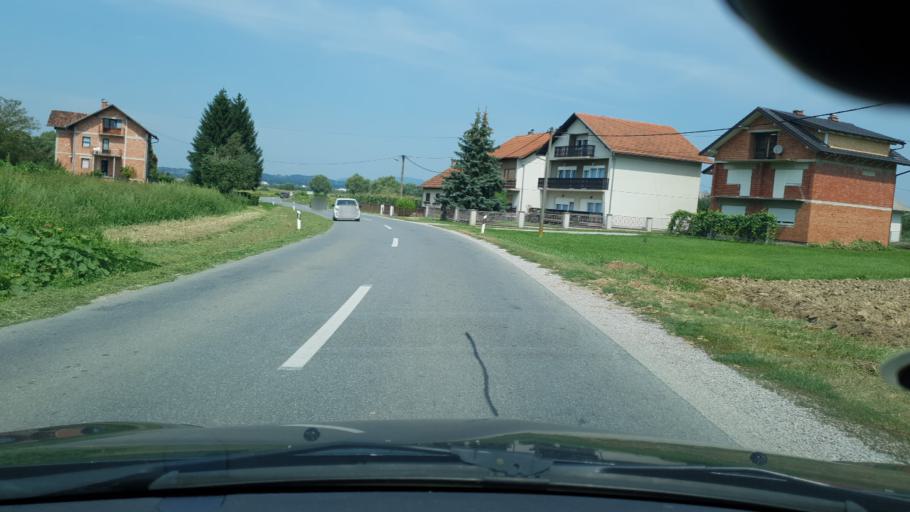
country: HR
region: Krapinsko-Zagorska
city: Marija Bistrica
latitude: 46.0326
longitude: 16.0968
